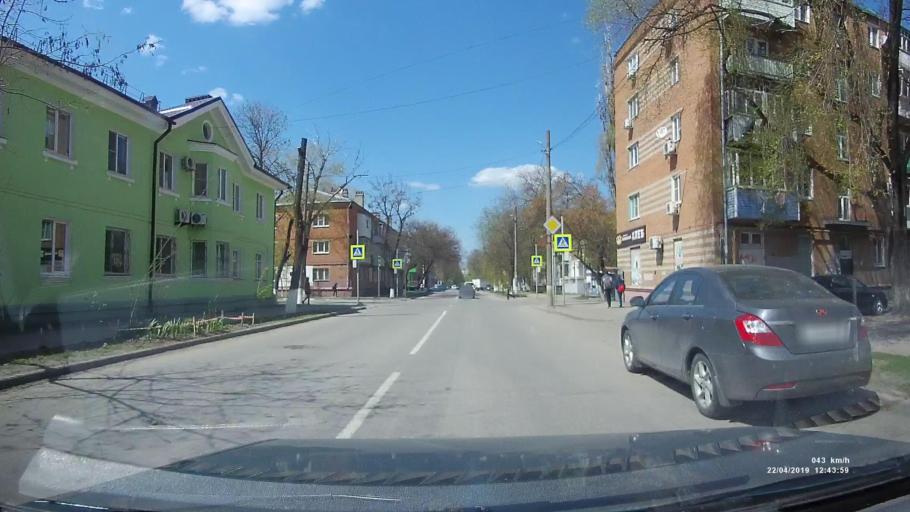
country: RU
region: Rostov
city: Azov
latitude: 47.1025
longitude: 39.4201
